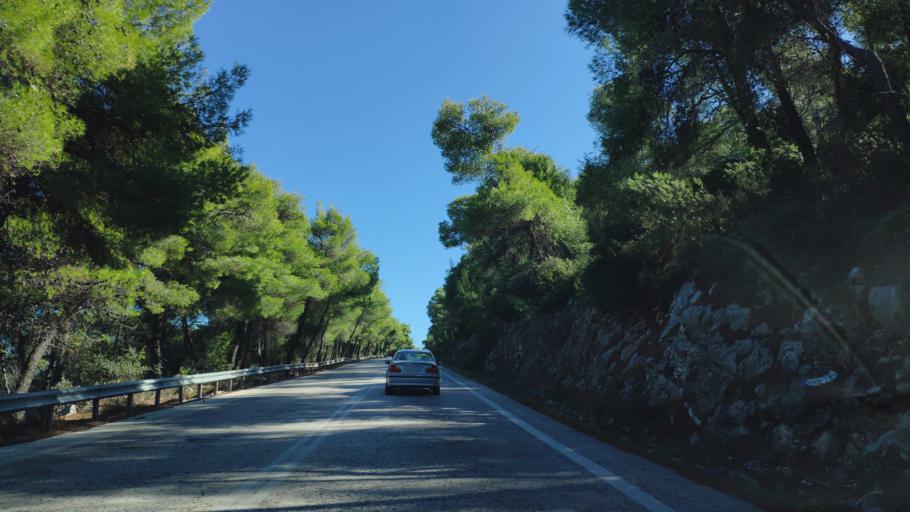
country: GR
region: Peloponnese
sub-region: Nomos Korinthias
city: Sofikon
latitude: 37.8265
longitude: 23.0956
